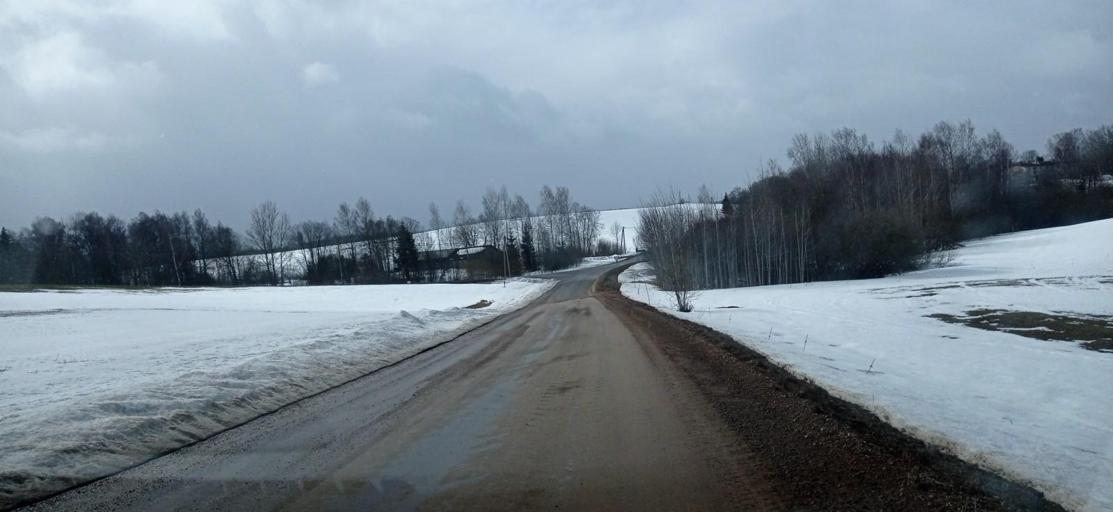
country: EE
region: Tartu
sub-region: Noo vald
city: Noo
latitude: 58.0876
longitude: 26.6580
